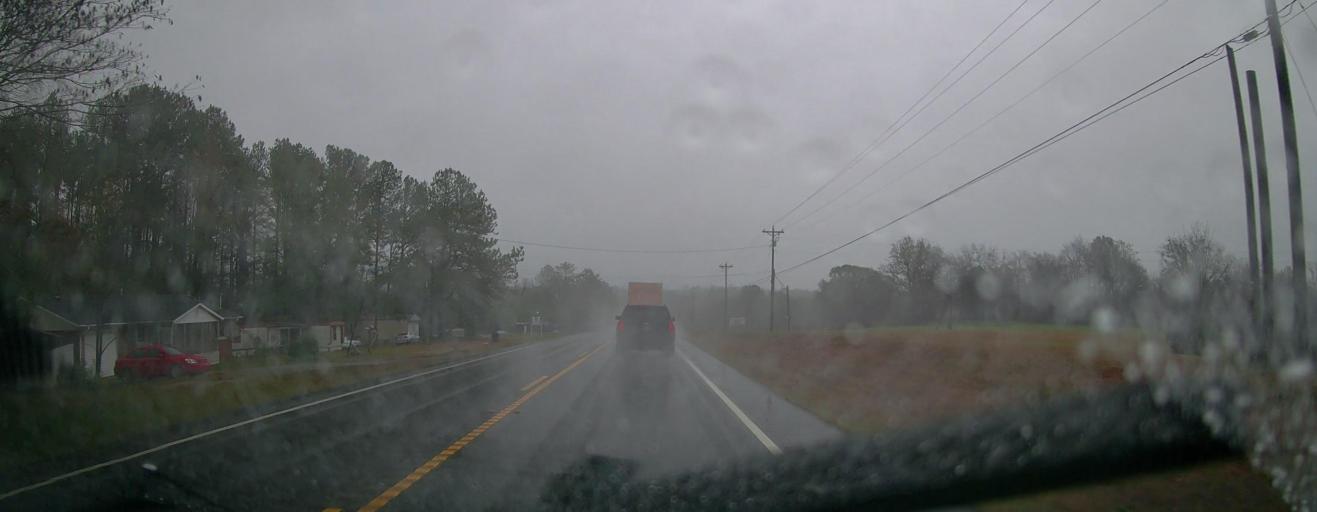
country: US
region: Georgia
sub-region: Putnam County
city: Eatonton
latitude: 33.2142
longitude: -83.4326
